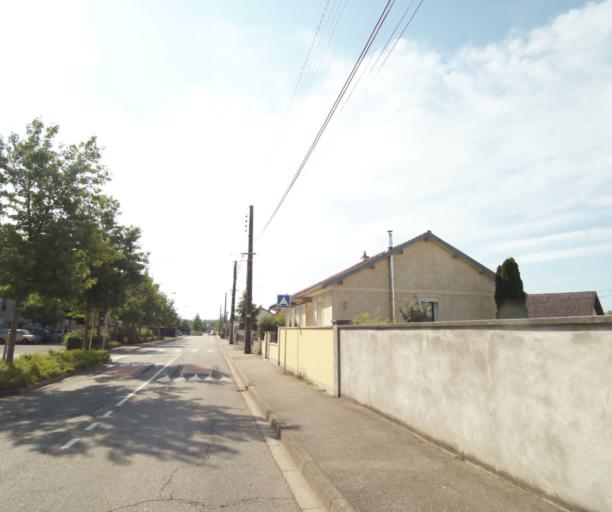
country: FR
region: Lorraine
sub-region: Departement de Meurthe-et-Moselle
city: Luneville
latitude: 48.5822
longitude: 6.5109
